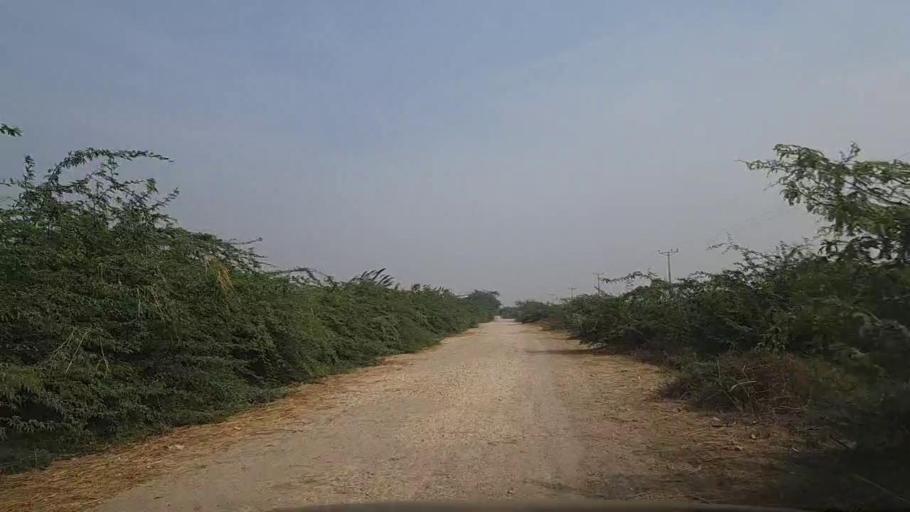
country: PK
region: Sindh
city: Mirpur Sakro
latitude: 24.4024
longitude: 67.7462
